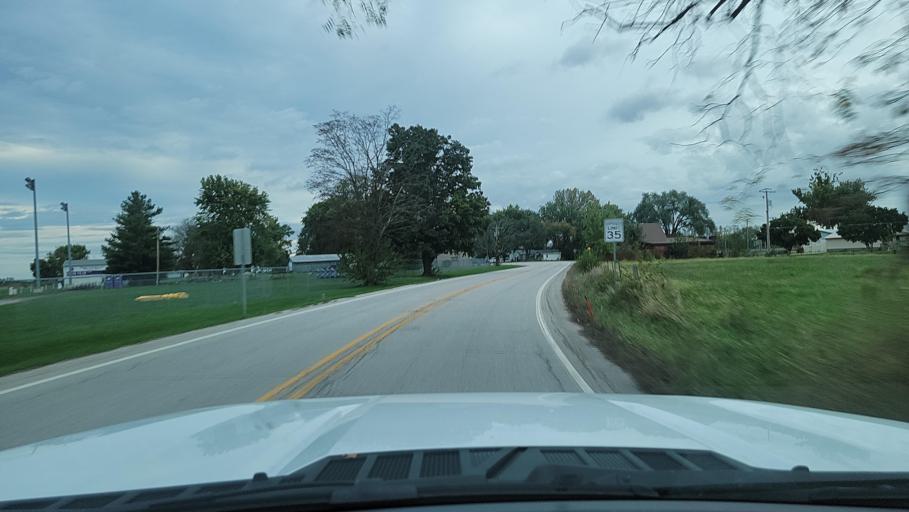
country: US
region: Illinois
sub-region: Schuyler County
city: Rushville
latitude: 40.1288
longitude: -90.5634
